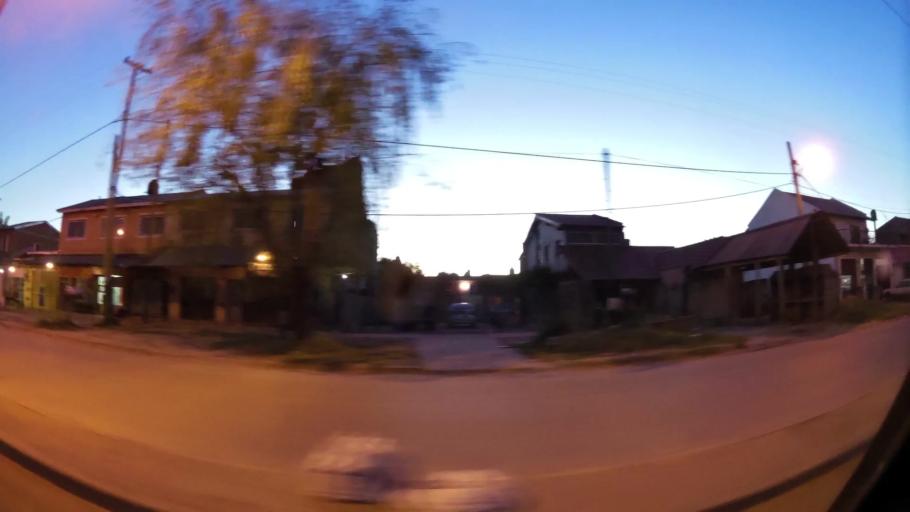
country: AR
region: Buenos Aires
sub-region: Partido de Almirante Brown
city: Adrogue
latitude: -34.7698
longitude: -58.3254
